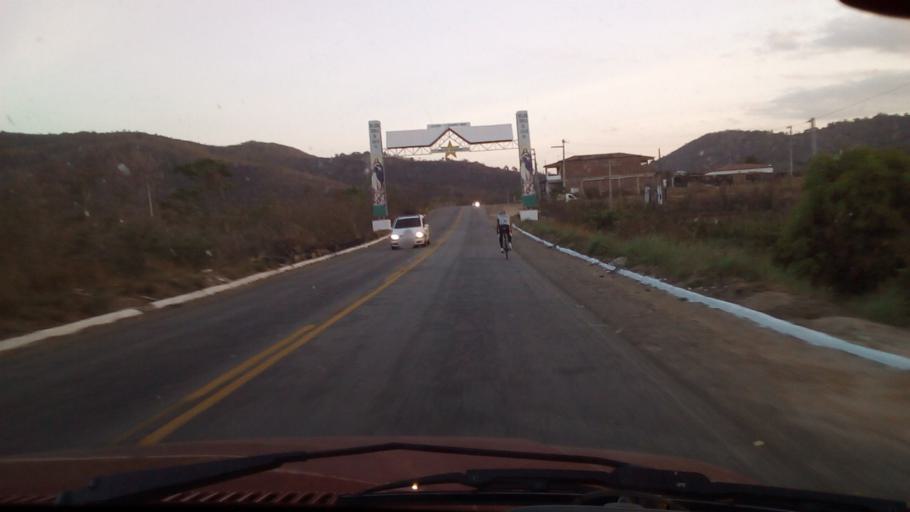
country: BR
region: Paraiba
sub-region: Belem
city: Belem
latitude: -6.7218
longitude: -35.5378
